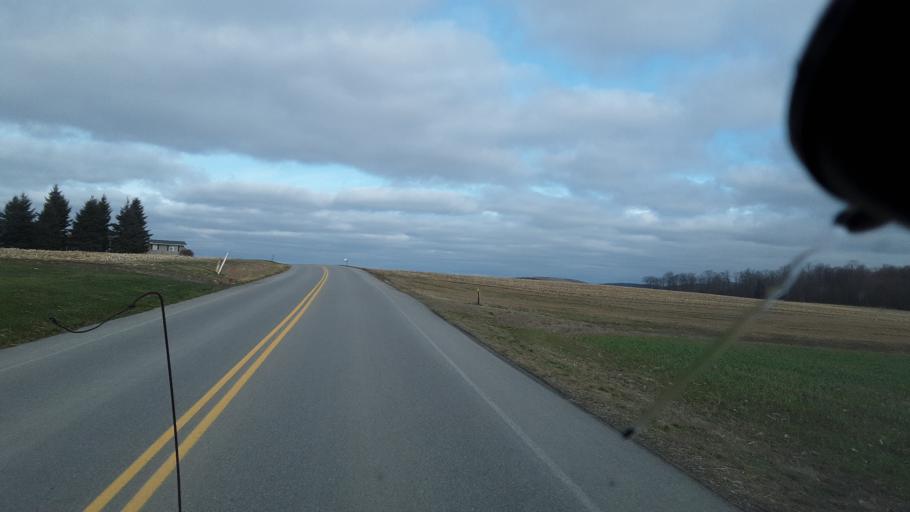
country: US
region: Pennsylvania
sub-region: Potter County
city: Galeton
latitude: 41.8783
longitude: -77.7626
